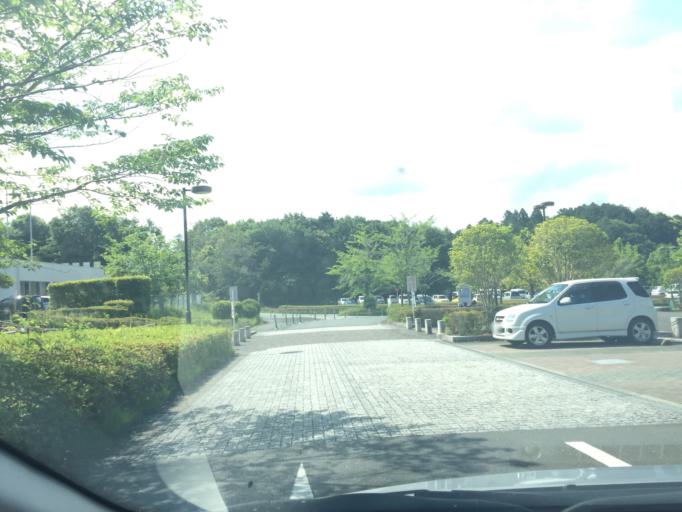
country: JP
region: Shizuoka
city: Kakegawa
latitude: 34.7857
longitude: 138.0022
